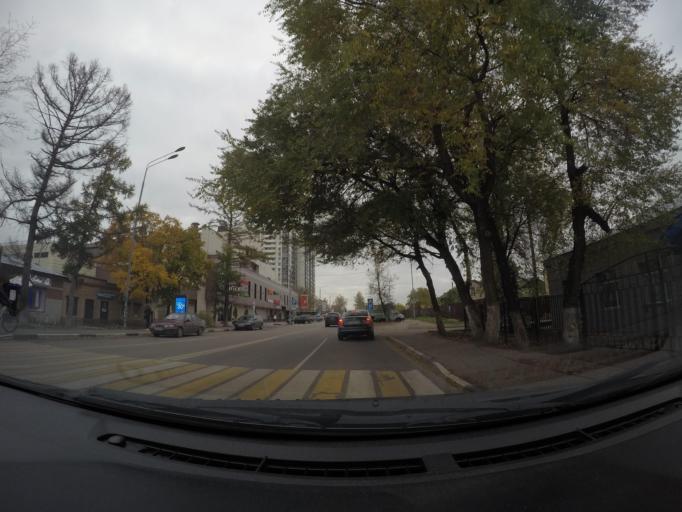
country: RU
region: Moskovskaya
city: Staraya Kupavna
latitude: 55.8032
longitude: 38.1814
